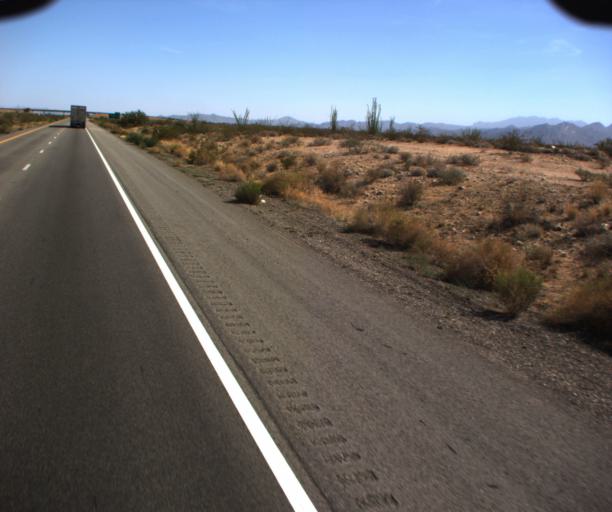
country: US
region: Arizona
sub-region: Mohave County
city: Kingman
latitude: 34.9074
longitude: -114.1536
